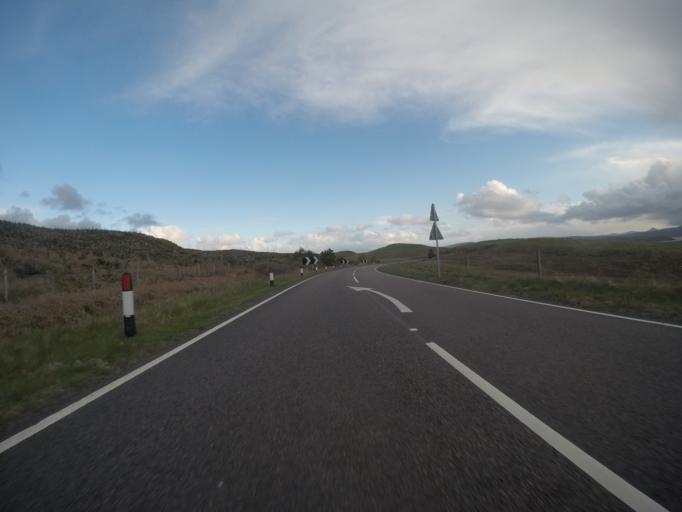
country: GB
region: Scotland
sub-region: Highland
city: Portree
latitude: 57.5494
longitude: -6.3637
